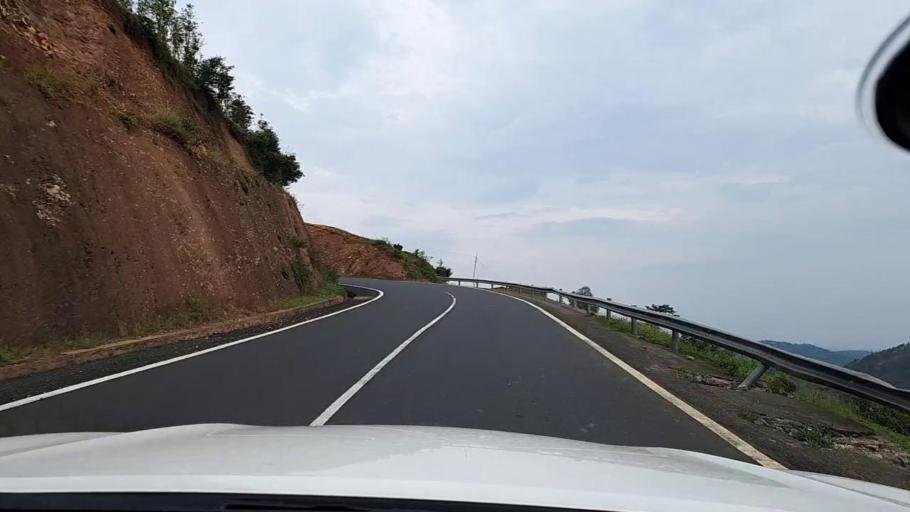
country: RW
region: Western Province
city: Kibuye
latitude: -2.1684
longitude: 29.2907
